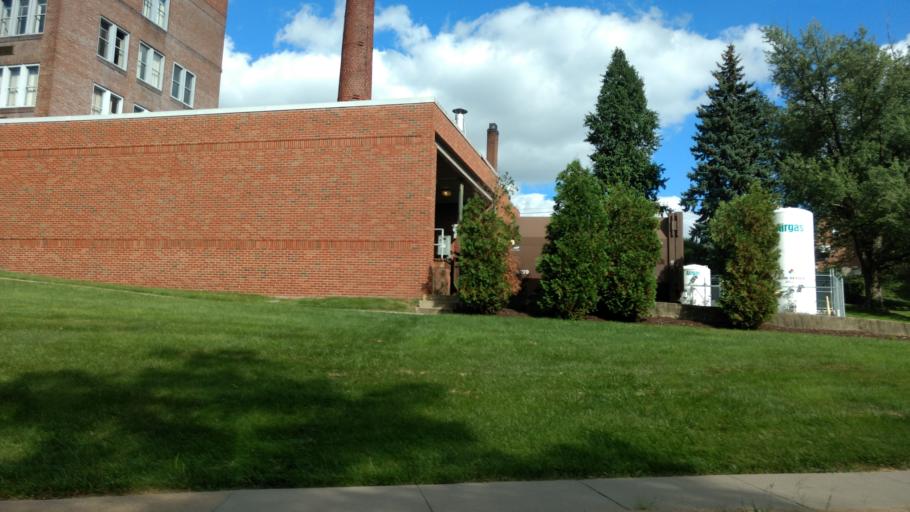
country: US
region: Pennsylvania
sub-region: Allegheny County
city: Avalon
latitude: 40.4945
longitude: -80.0613
